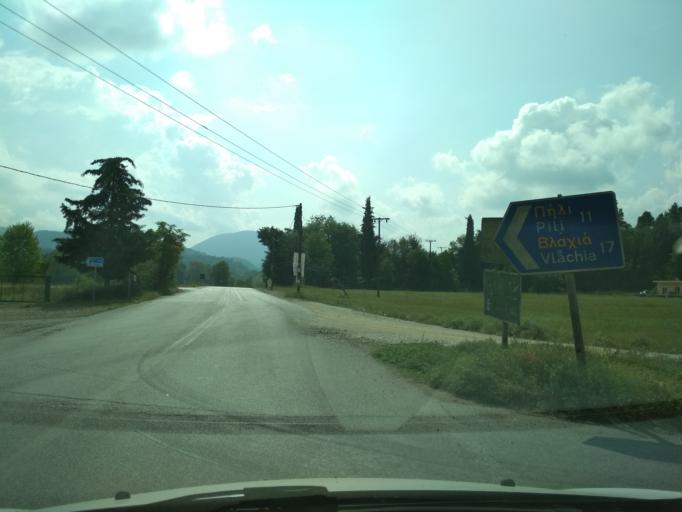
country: GR
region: Central Greece
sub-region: Nomos Evvoias
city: Prokopion
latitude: 38.7340
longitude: 23.4945
